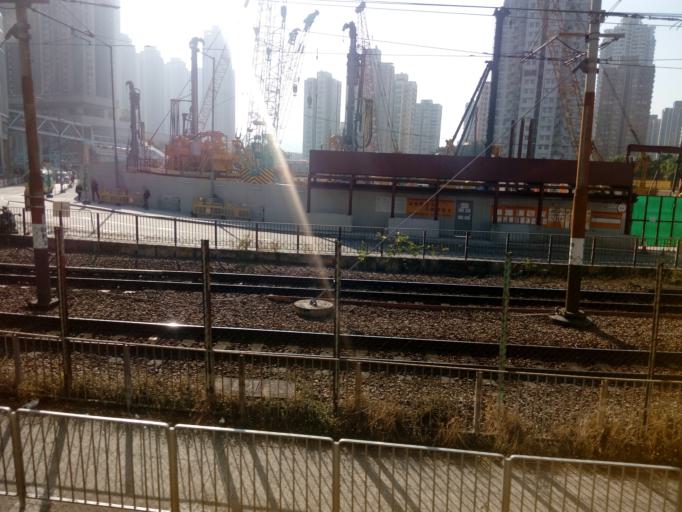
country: HK
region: Yuen Long
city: Yuen Long Kau Hui
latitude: 22.4456
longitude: 114.0334
